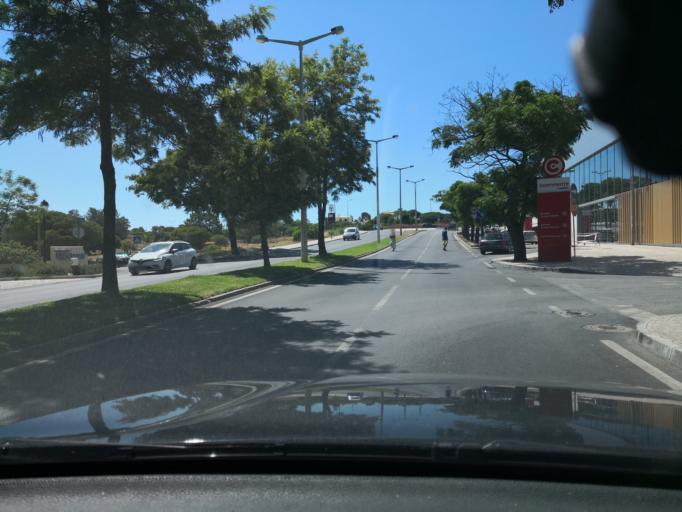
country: PT
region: Faro
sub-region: Loule
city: Quarteira
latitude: 37.0751
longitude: -8.0953
